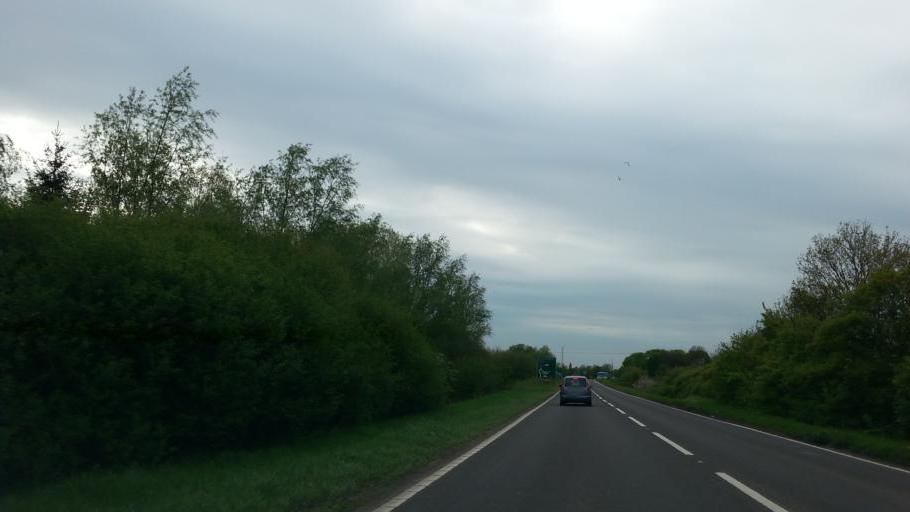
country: GB
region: England
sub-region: Cambridgeshire
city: March
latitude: 52.5221
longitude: 0.0869
